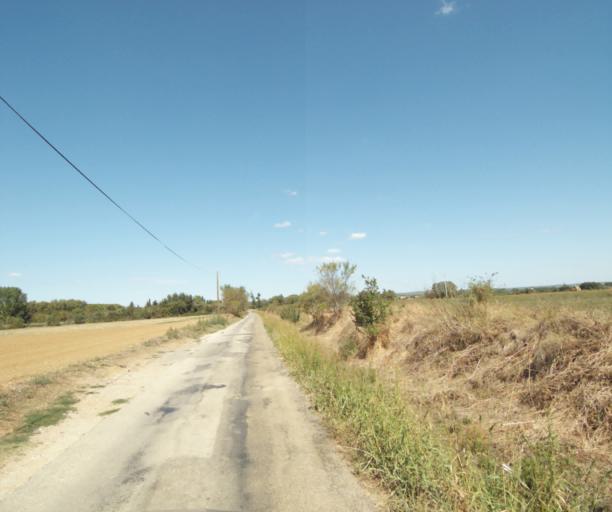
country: FR
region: Languedoc-Roussillon
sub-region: Departement du Gard
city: Rodilhan
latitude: 43.8141
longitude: 4.4162
